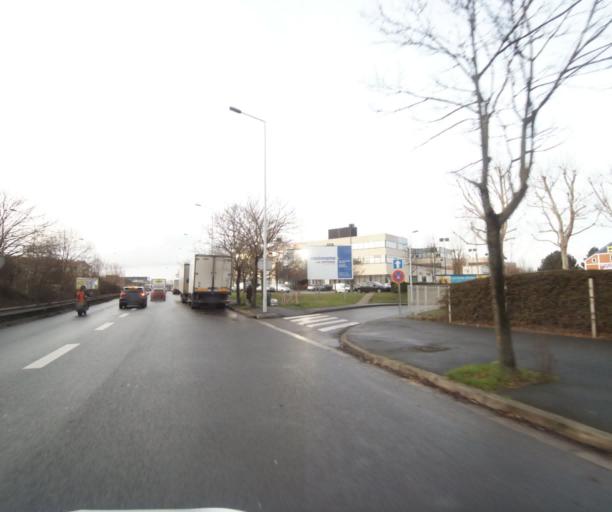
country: FR
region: Ile-de-France
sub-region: Departement du Val-d'Oise
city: Bezons
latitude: 48.9176
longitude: 2.2218
